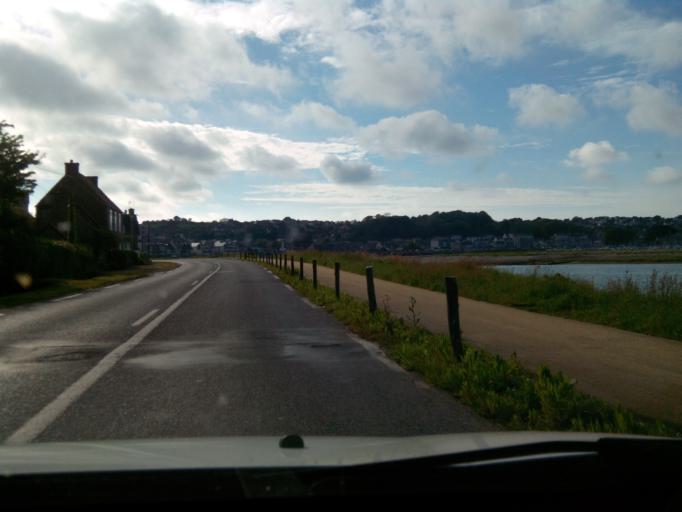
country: FR
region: Brittany
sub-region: Departement des Cotes-d'Armor
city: Perros-Guirec
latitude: 48.7976
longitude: -3.4359
